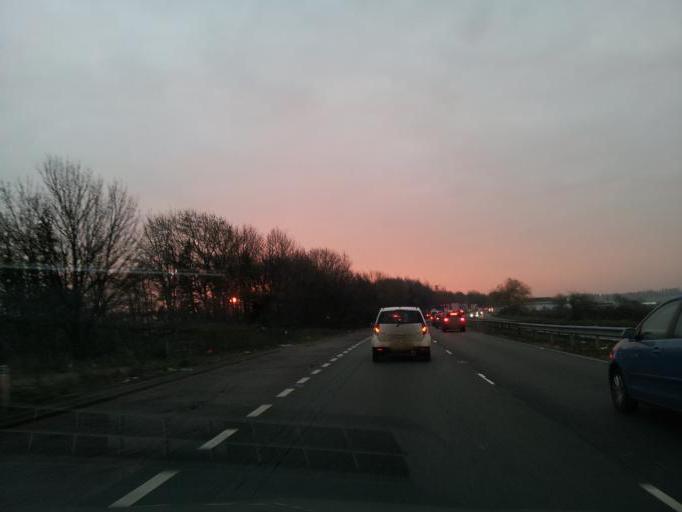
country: GB
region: England
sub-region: Peterborough
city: Thornhaugh
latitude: 52.6006
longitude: -0.4230
